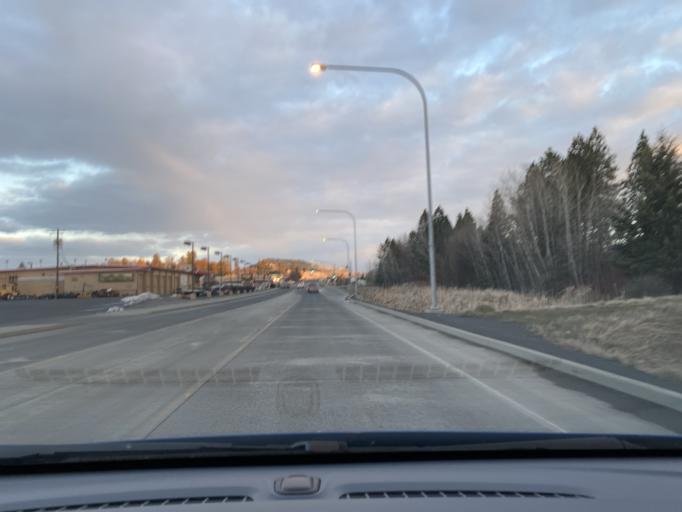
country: US
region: Idaho
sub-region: Latah County
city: Moscow
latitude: 46.7218
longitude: -116.9883
